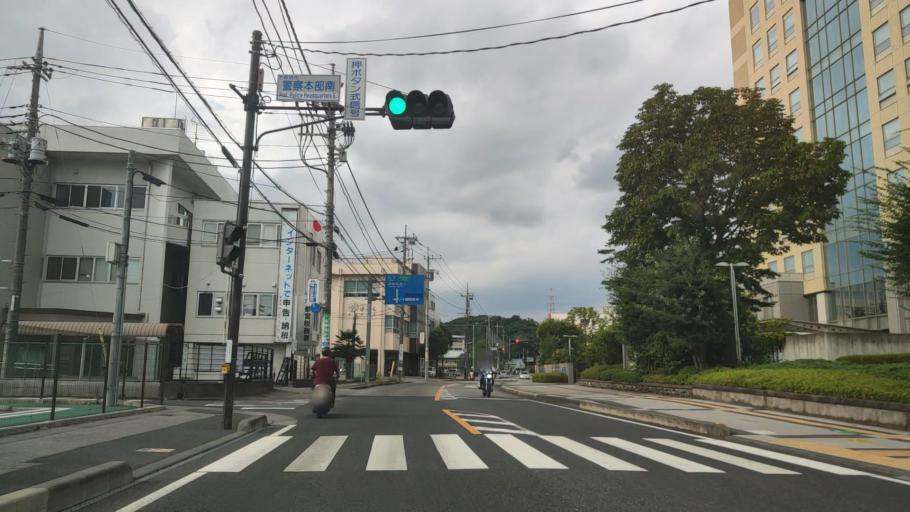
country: JP
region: Tochigi
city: Utsunomiya-shi
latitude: 36.5662
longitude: 139.8825
